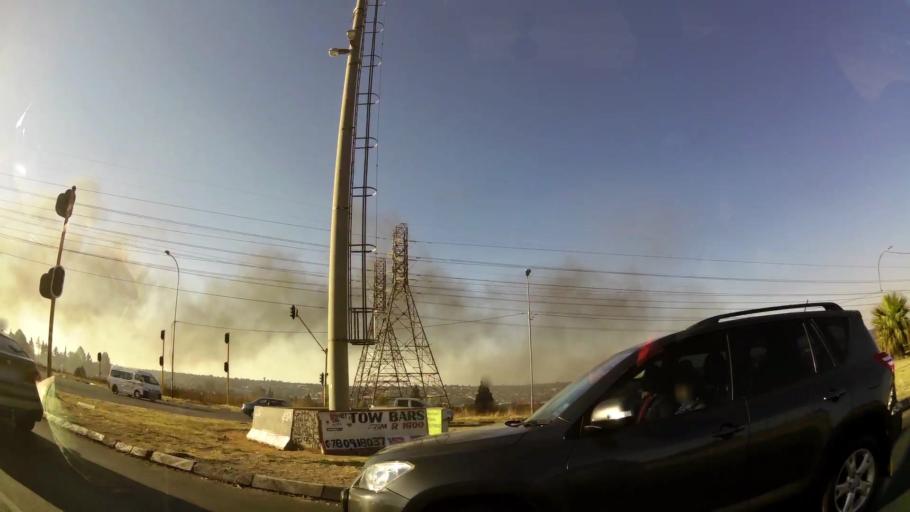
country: ZA
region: Gauteng
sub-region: City of Johannesburg Metropolitan Municipality
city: Roodepoort
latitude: -26.1773
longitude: 27.8810
